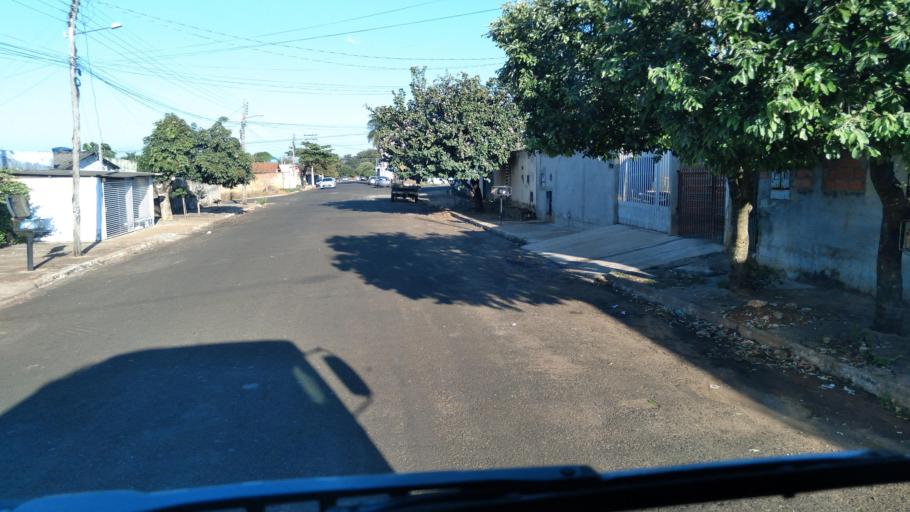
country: BR
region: Goias
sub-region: Mineiros
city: Mineiros
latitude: -17.5752
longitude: -52.5639
